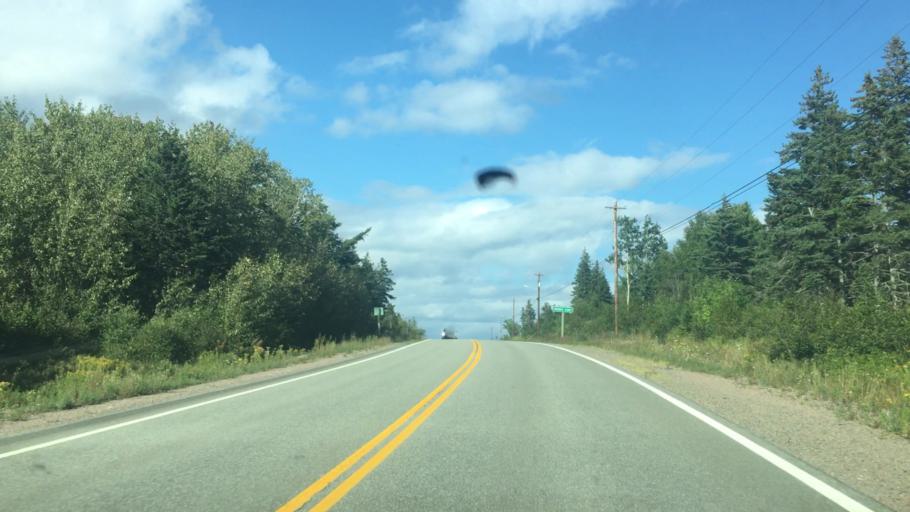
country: CA
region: Nova Scotia
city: Sydney
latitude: 45.8550
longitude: -60.6304
